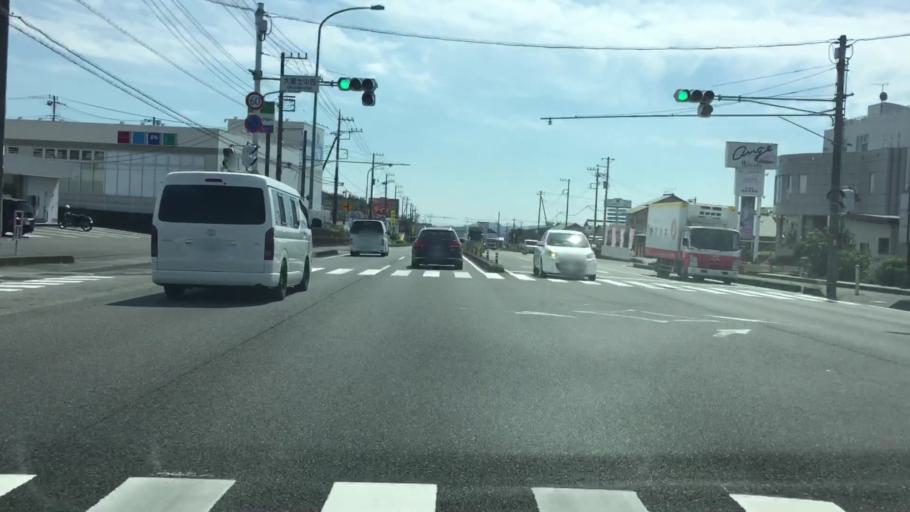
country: JP
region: Shizuoka
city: Fujinomiya
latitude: 35.2534
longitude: 138.6161
